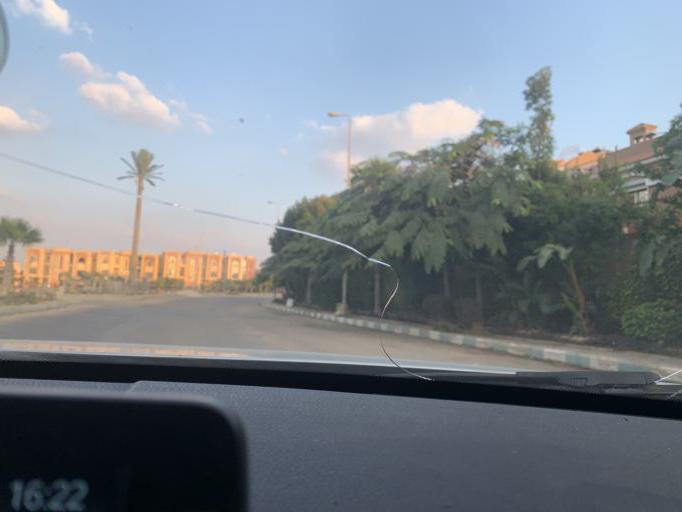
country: EG
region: Muhafazat al Qalyubiyah
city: Al Khankah
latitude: 30.0163
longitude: 31.4847
